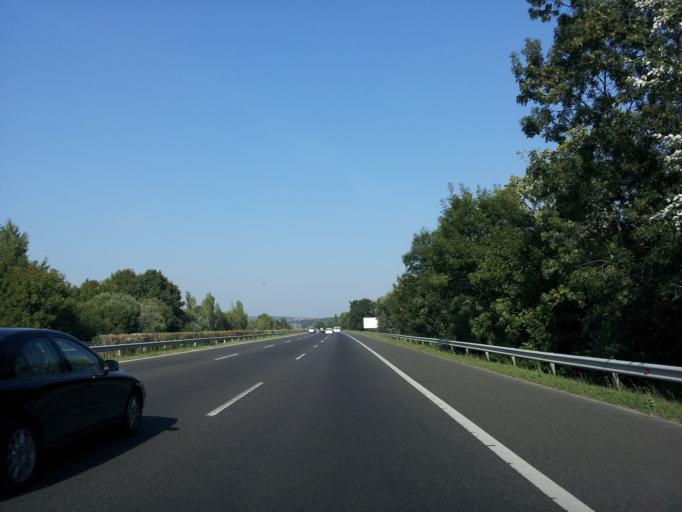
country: HU
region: Fejer
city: Pakozd
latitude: 47.2131
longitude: 18.5512
